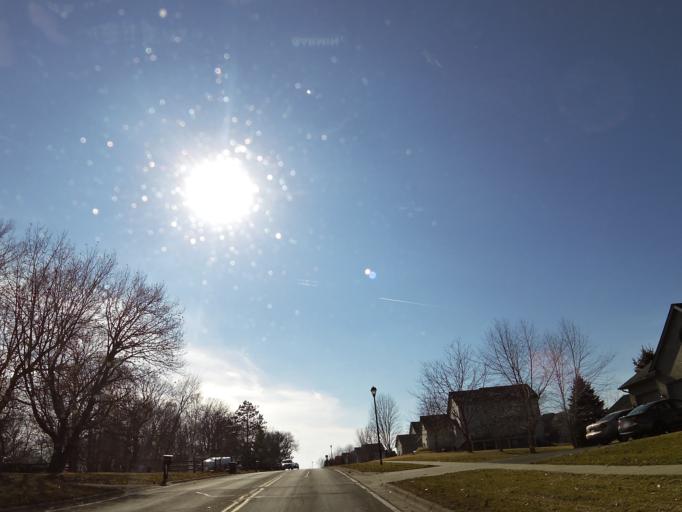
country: US
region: Minnesota
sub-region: Scott County
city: Prior Lake
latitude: 44.7170
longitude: -93.4541
